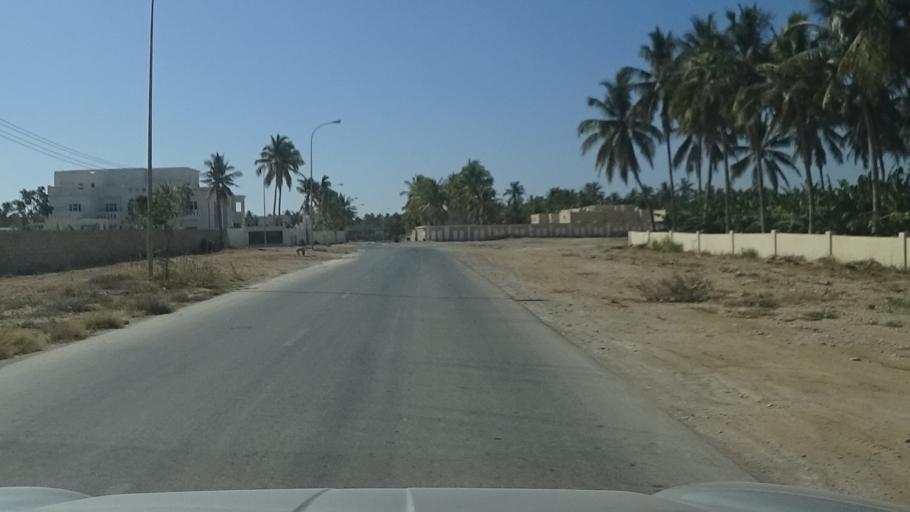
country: OM
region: Zufar
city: Salalah
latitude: 17.0352
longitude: 54.1538
